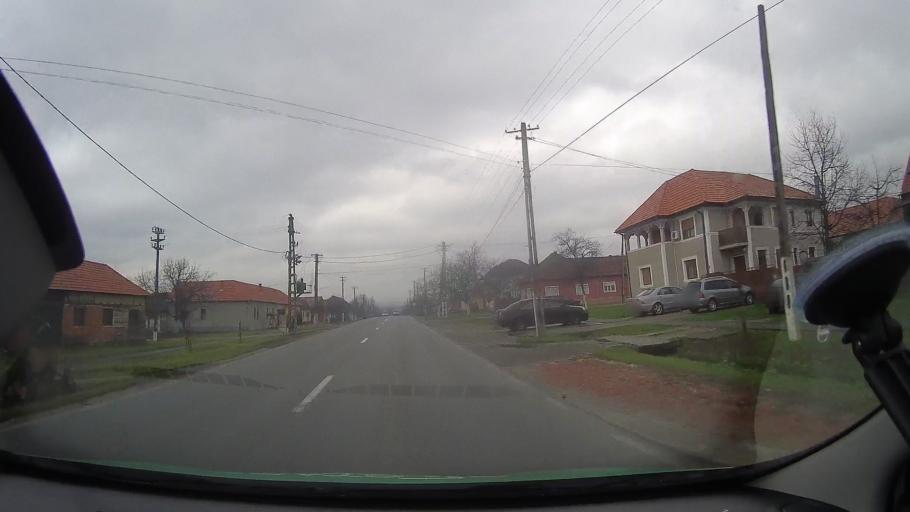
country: RO
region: Arad
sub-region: Comuna Almas
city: Almas
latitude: 46.2866
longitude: 22.2310
